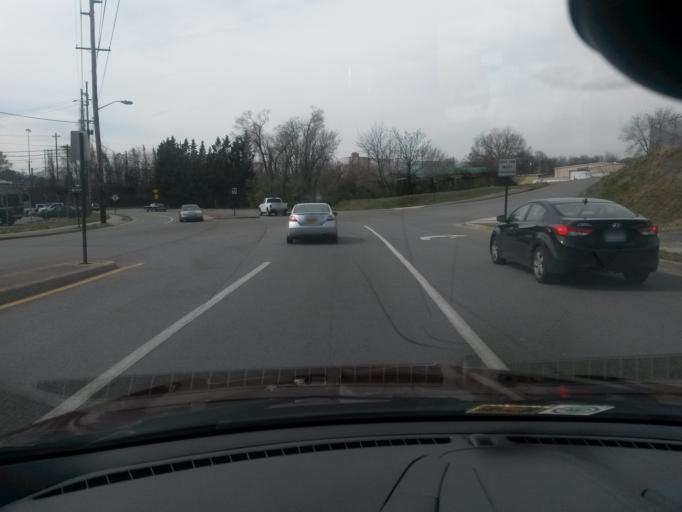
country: US
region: Virginia
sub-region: City of Roanoke
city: Roanoke
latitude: 37.2818
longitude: -79.9773
